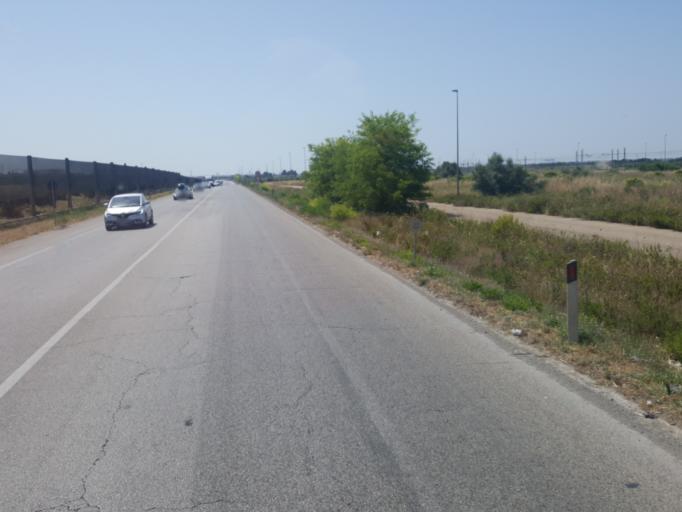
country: IT
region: Apulia
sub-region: Provincia di Taranto
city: Massafra
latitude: 40.5553
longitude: 17.1385
